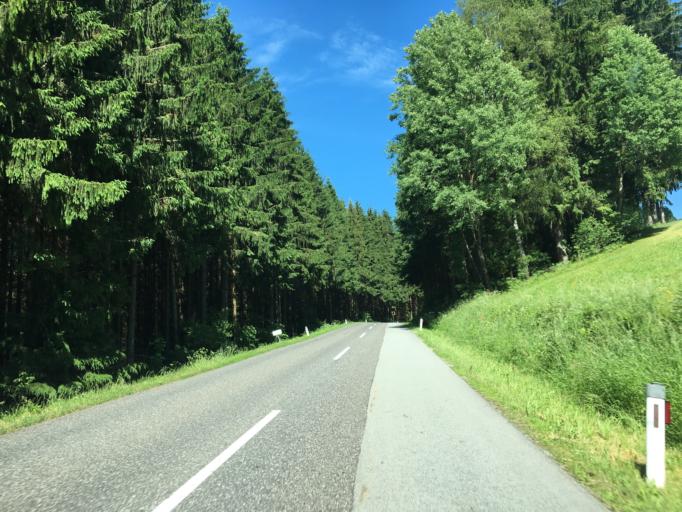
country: AT
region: Upper Austria
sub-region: Politischer Bezirk Urfahr-Umgebung
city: Zwettl an der Rodl
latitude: 48.4446
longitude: 14.2544
